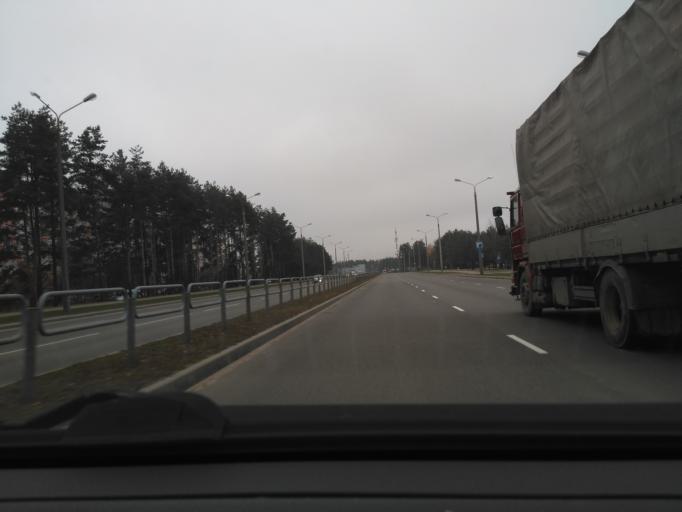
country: BY
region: Minsk
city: Horad Barysaw
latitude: 54.2000
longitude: 28.4769
